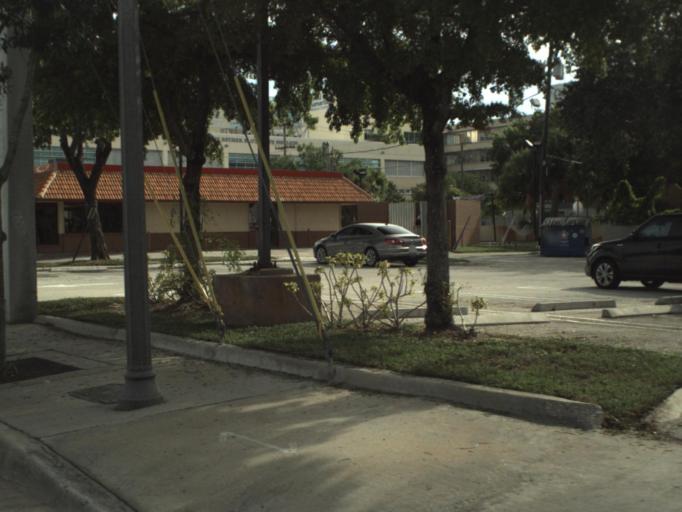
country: US
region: Florida
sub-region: Palm Beach County
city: West Palm Beach
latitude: 26.7236
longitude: -80.0532
